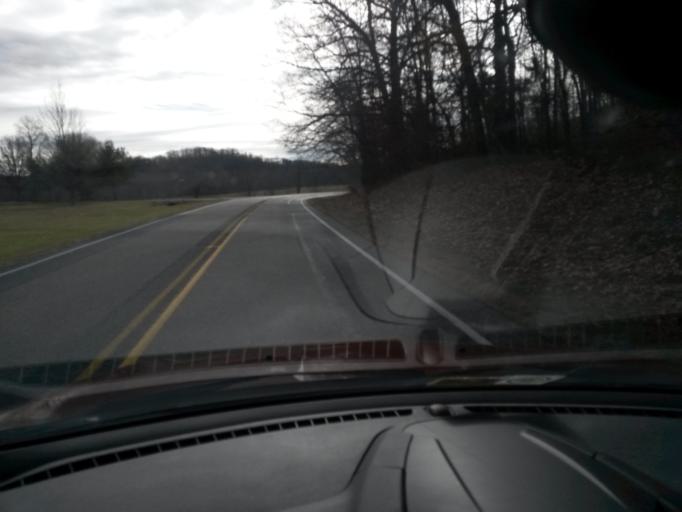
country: US
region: Virginia
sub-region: City of Staunton
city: Staunton
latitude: 38.1947
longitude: -79.2196
